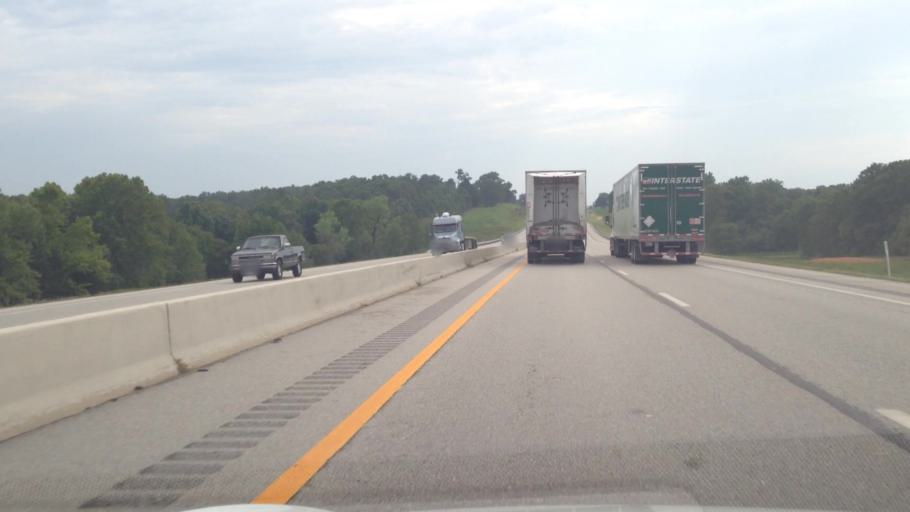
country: US
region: Kansas
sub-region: Cherokee County
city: Galena
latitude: 36.9786
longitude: -94.6396
